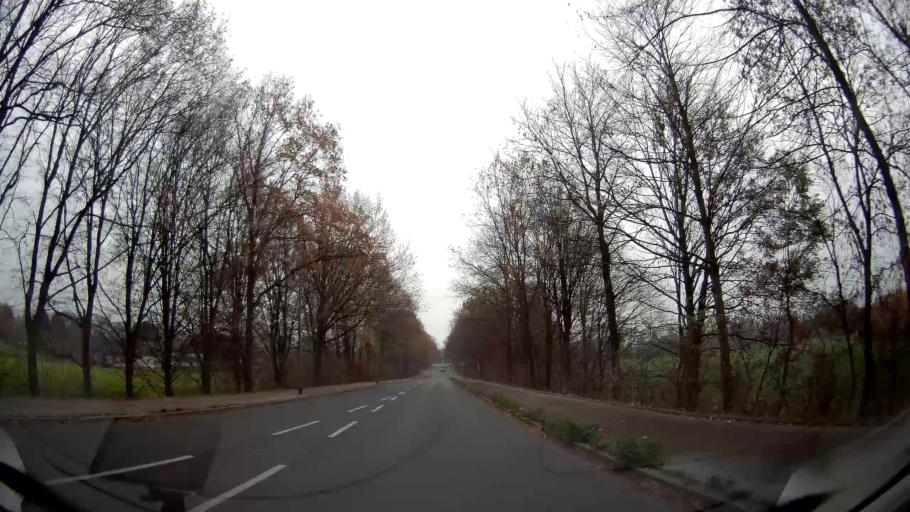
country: DE
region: North Rhine-Westphalia
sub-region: Regierungsbezirk Munster
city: Gladbeck
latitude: 51.5781
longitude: 7.0187
